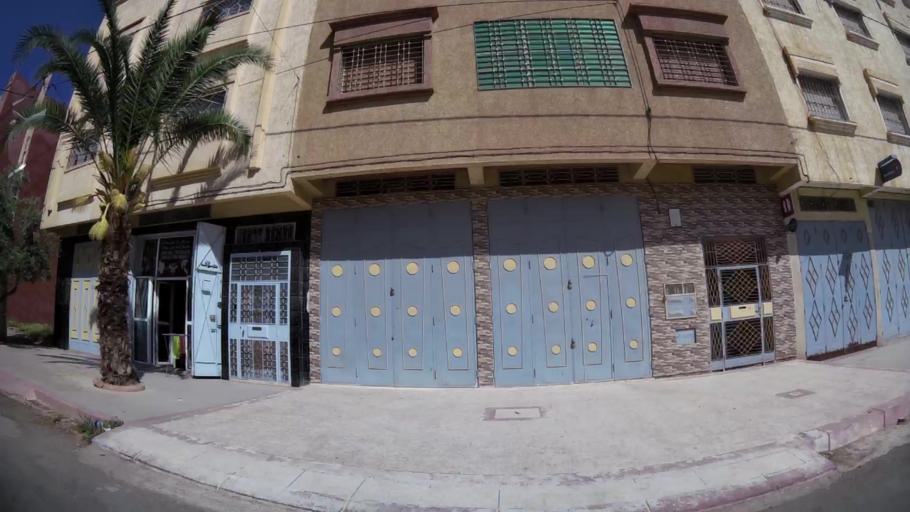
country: MA
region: Oriental
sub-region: Oujda-Angad
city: Oujda
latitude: 34.6784
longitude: -1.9333
